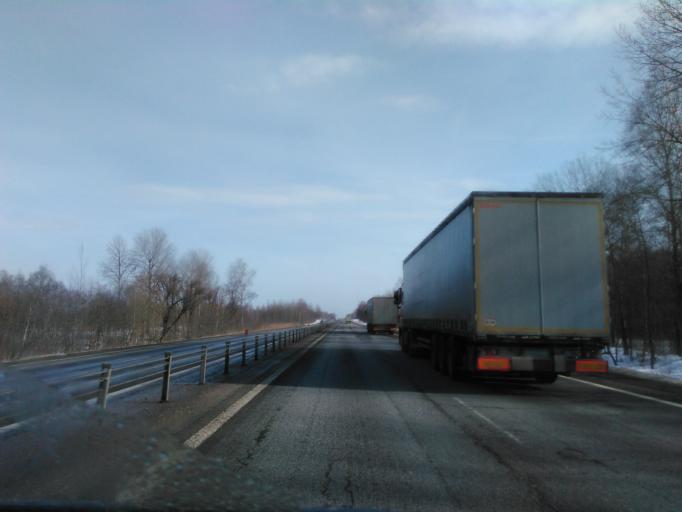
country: BY
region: Vitebsk
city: Dubrowna
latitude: 54.6837
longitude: 30.7873
